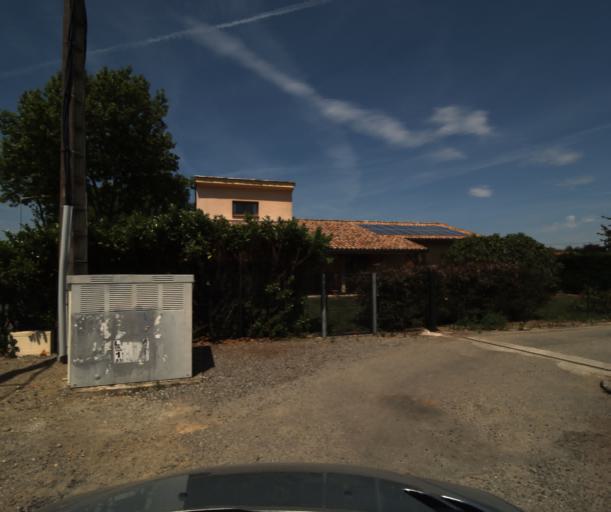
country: FR
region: Midi-Pyrenees
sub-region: Departement de la Haute-Garonne
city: Labastidette
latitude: 43.4578
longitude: 1.2439
